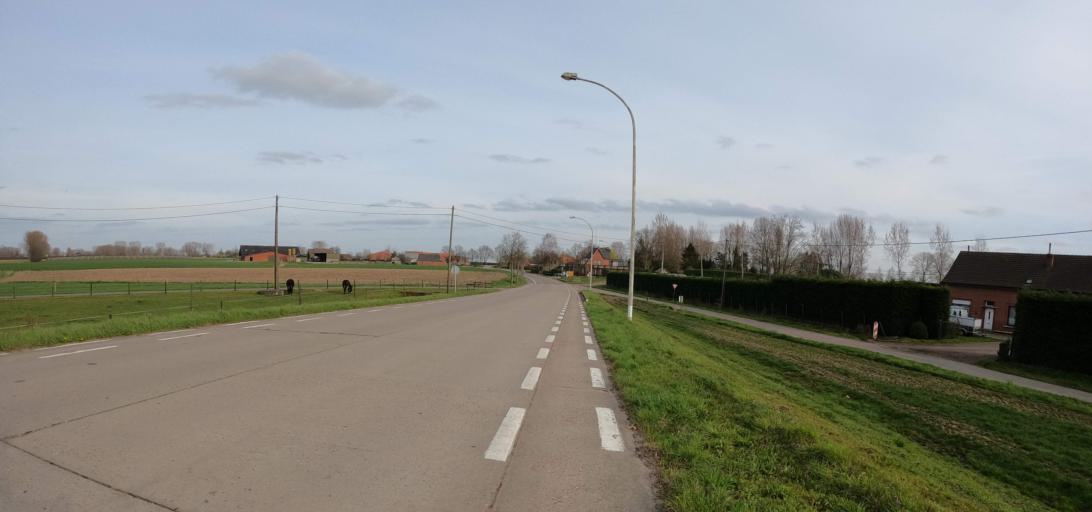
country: BE
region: Flanders
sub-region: Provincie Oost-Vlaanderen
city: Beveren
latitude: 51.1702
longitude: 4.2587
